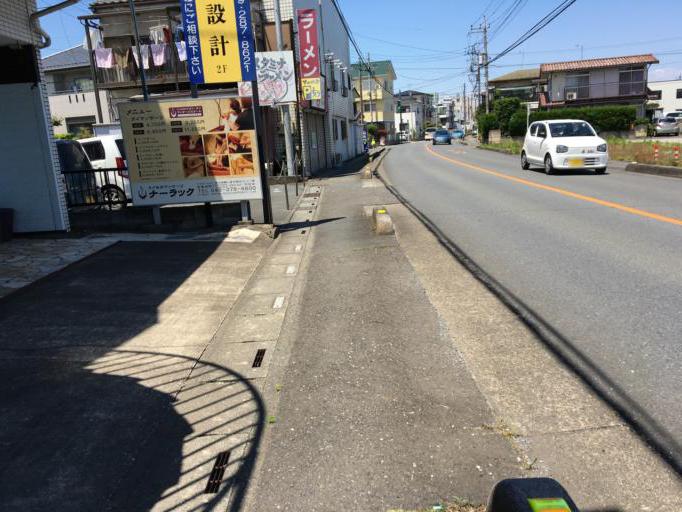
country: JP
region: Saitama
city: Sakado
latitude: 35.9453
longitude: 139.3870
